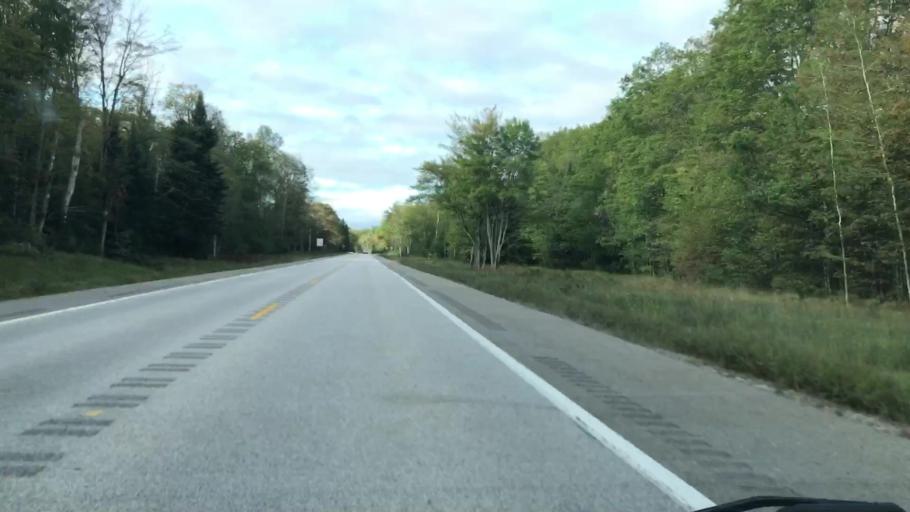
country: US
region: Michigan
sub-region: Luce County
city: Newberry
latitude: 46.3372
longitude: -85.0452
